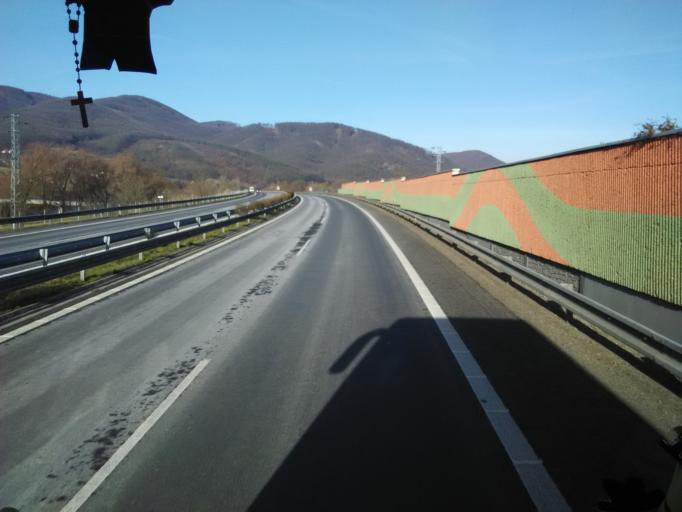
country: SK
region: Banskobystricky
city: Nova Bana
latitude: 48.3797
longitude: 18.6099
